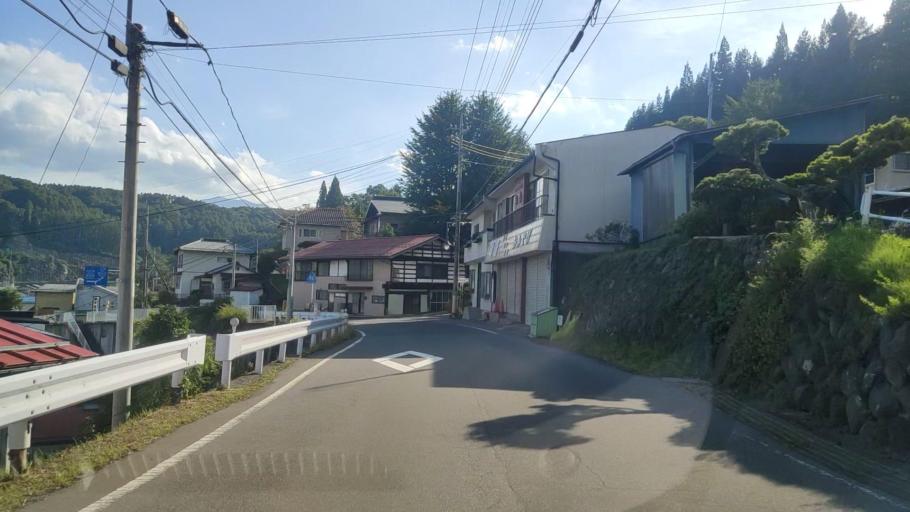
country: JP
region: Nagano
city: Komoro
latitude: 36.5356
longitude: 138.5494
